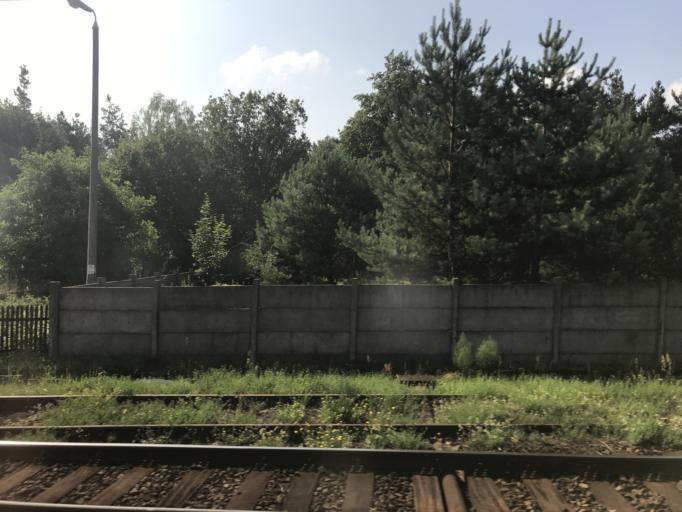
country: PL
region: Kujawsko-Pomorskie
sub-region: Powiat chelminski
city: Chelmno
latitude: 53.4068
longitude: 18.3432
